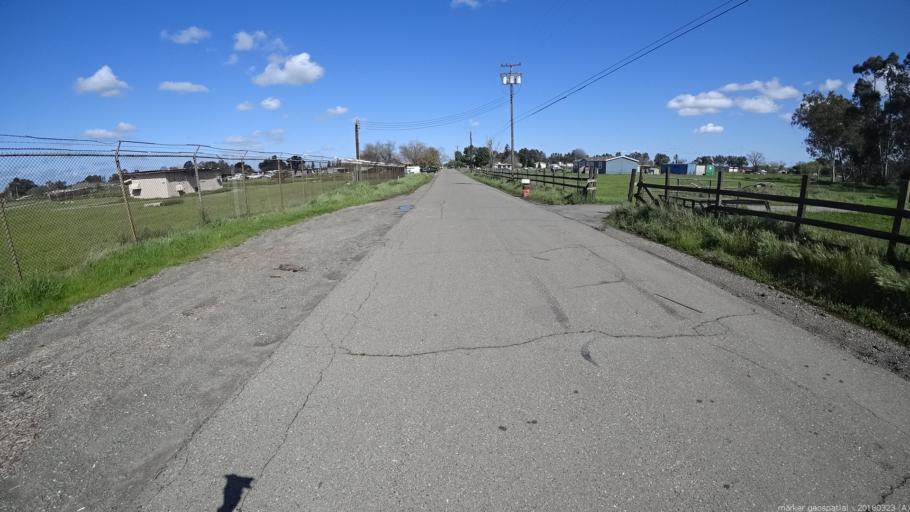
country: US
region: California
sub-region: Sacramento County
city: North Highlands
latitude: 38.6719
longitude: -121.4107
